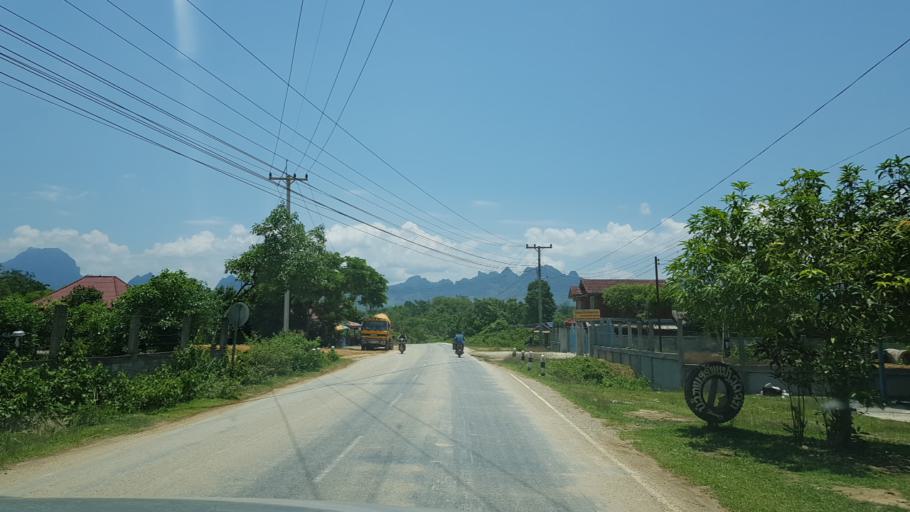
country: LA
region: Vientiane
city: Muang Kasi
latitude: 19.2528
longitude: 102.2425
